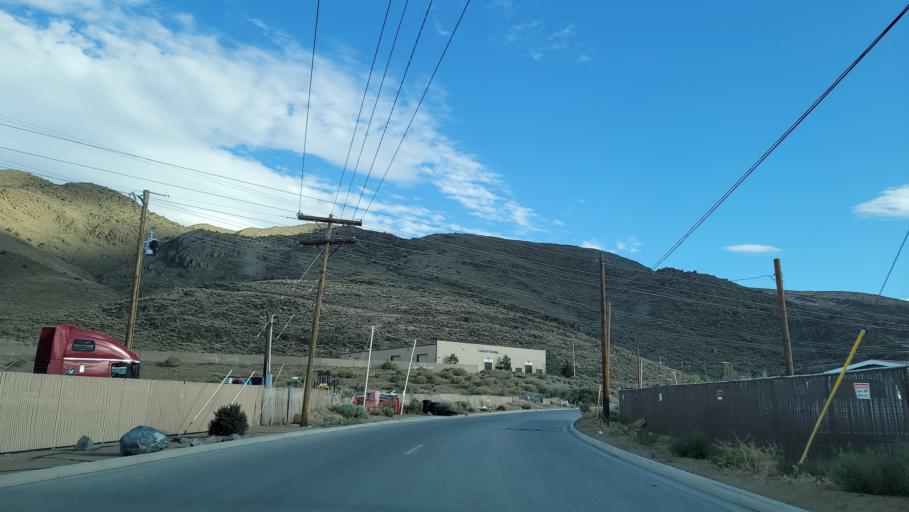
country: US
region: Nevada
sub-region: Washoe County
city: Spanish Springs
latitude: 39.5489
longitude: -119.5531
